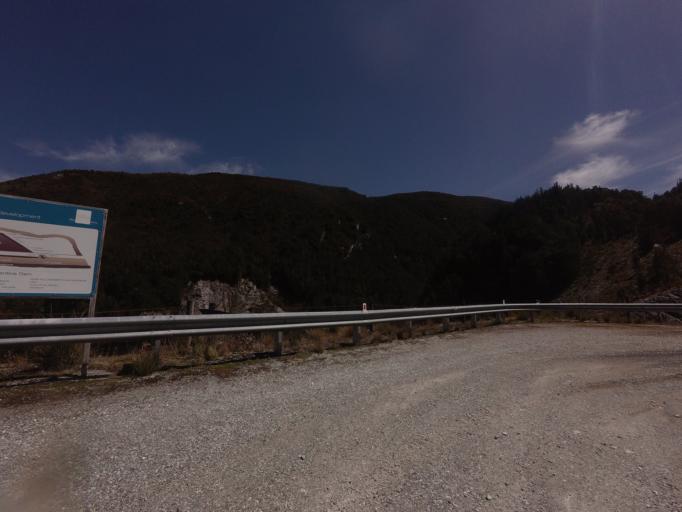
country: AU
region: Tasmania
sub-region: West Coast
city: Queenstown
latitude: -42.7758
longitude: 145.9837
